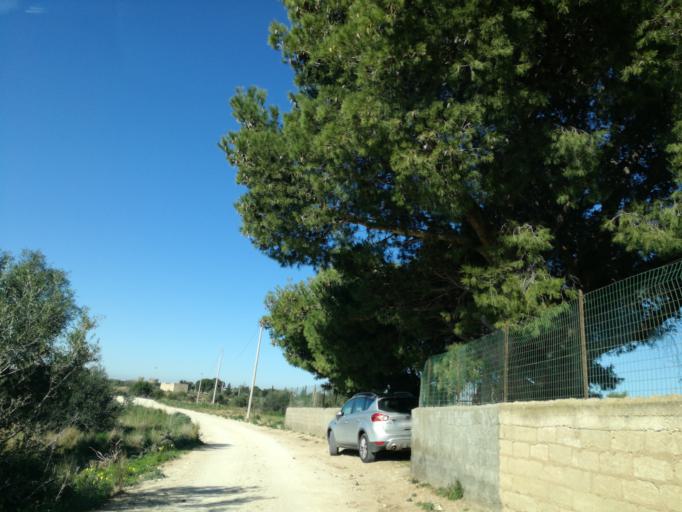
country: IT
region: Sicily
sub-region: Provincia di Caltanissetta
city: Niscemi
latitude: 37.0554
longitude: 14.3623
